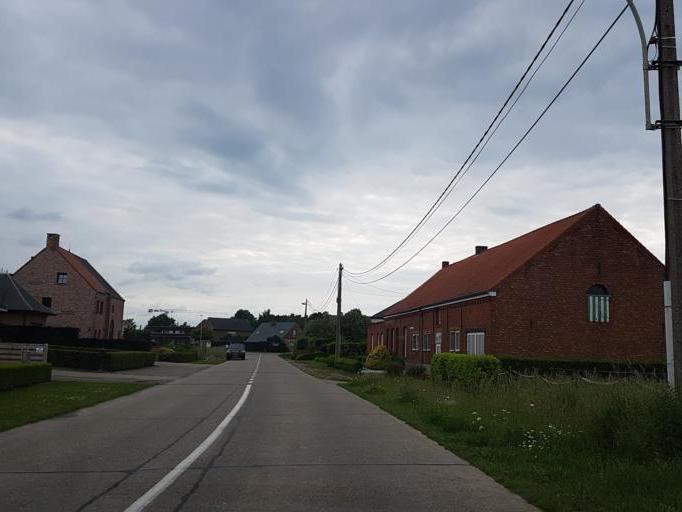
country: BE
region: Flanders
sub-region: Provincie Antwerpen
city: Rijkevorsel
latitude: 51.3536
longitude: 4.7647
